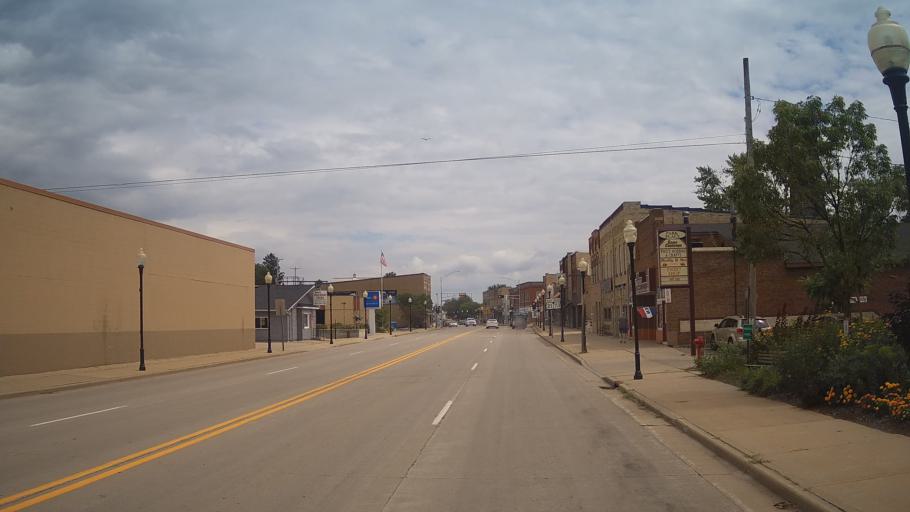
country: US
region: Wisconsin
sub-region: Waushara County
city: Wautoma
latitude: 44.0757
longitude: -89.2931
